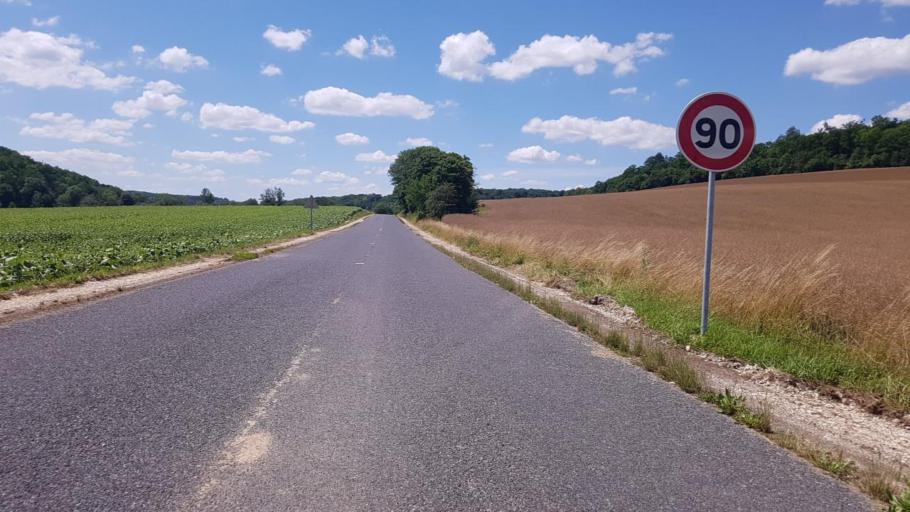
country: FR
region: Lorraine
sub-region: Departement de la Meuse
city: Ligny-en-Barrois
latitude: 48.6477
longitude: 5.4118
